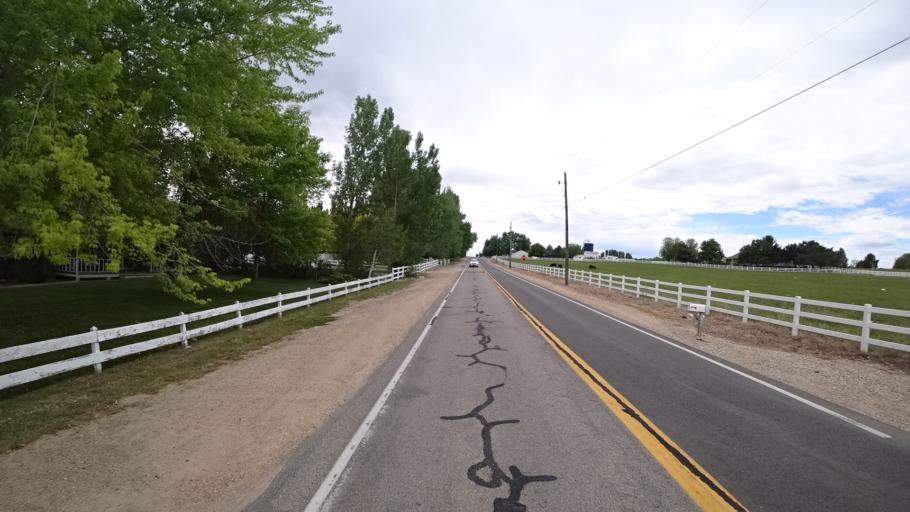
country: US
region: Idaho
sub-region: Ada County
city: Meridian
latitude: 43.5779
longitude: -116.4137
